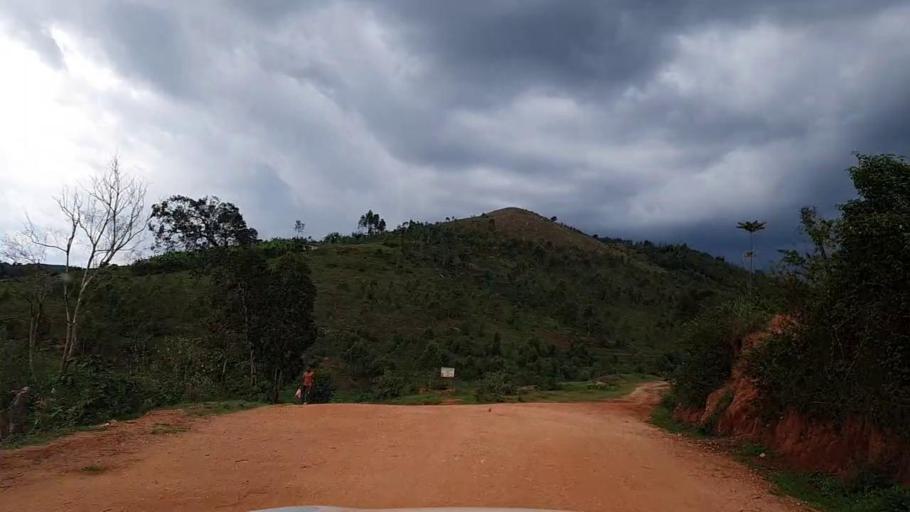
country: RW
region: Southern Province
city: Nyanza
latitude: -2.3929
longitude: 29.6912
